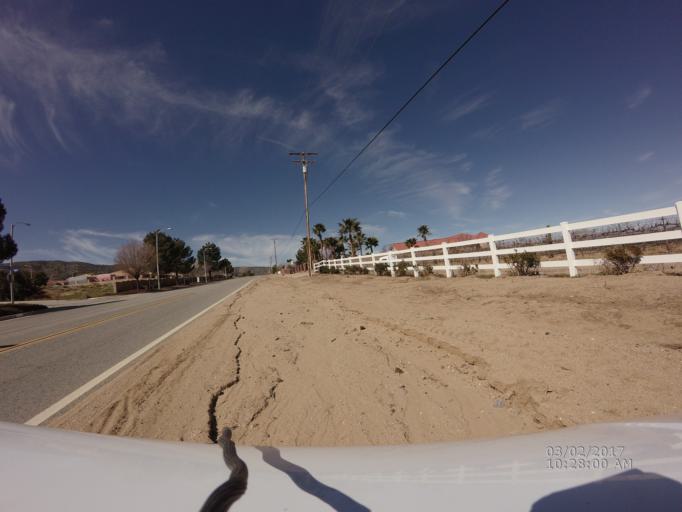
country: US
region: California
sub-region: Los Angeles County
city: Quartz Hill
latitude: 34.6382
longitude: -118.2387
